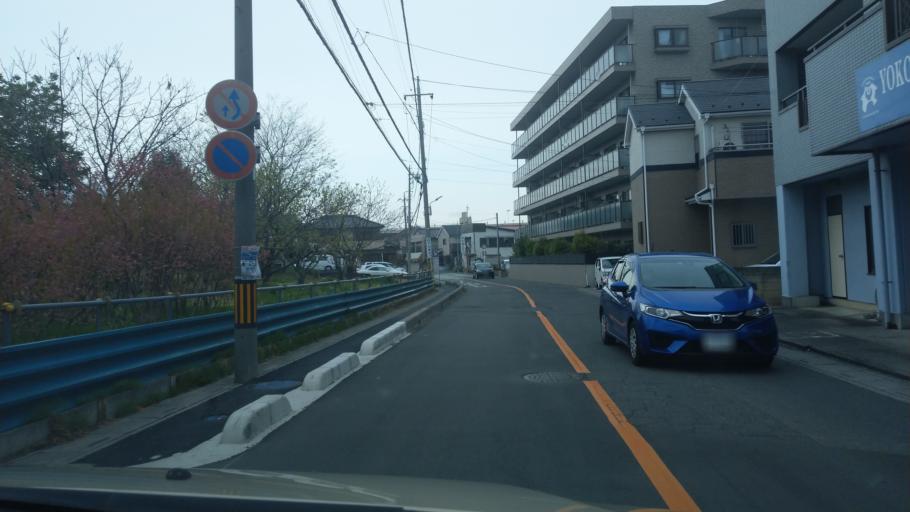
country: JP
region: Saitama
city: Ageoshimo
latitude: 35.9524
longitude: 139.5985
